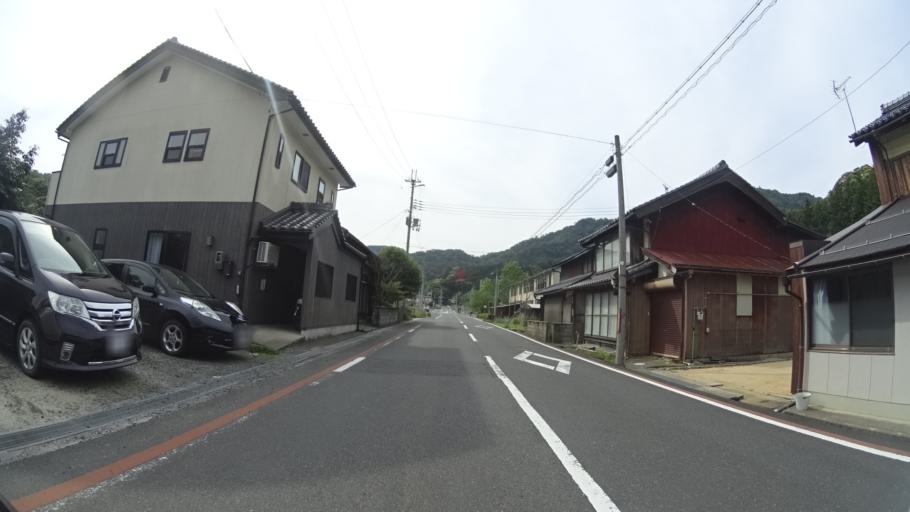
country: JP
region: Kyoto
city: Miyazu
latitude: 35.6725
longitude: 135.2747
